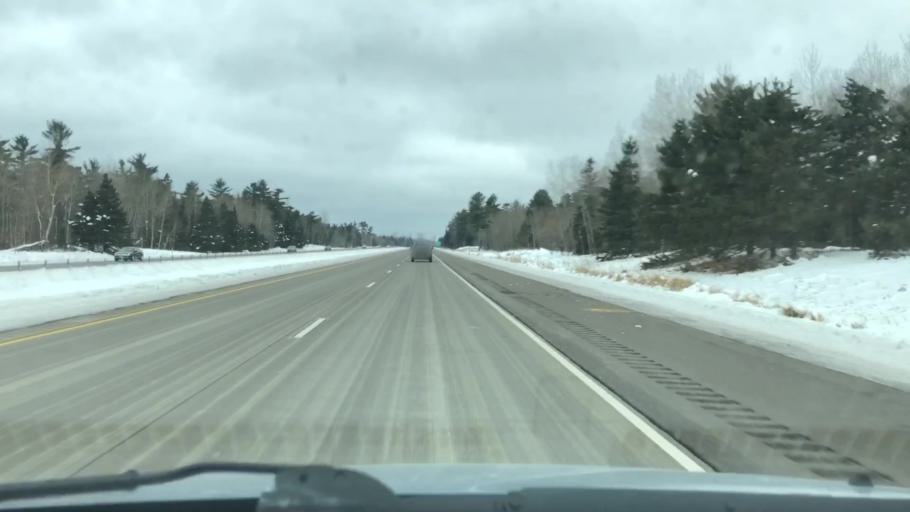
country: US
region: Minnesota
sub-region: Carlton County
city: Esko
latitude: 46.6993
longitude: -92.3268
